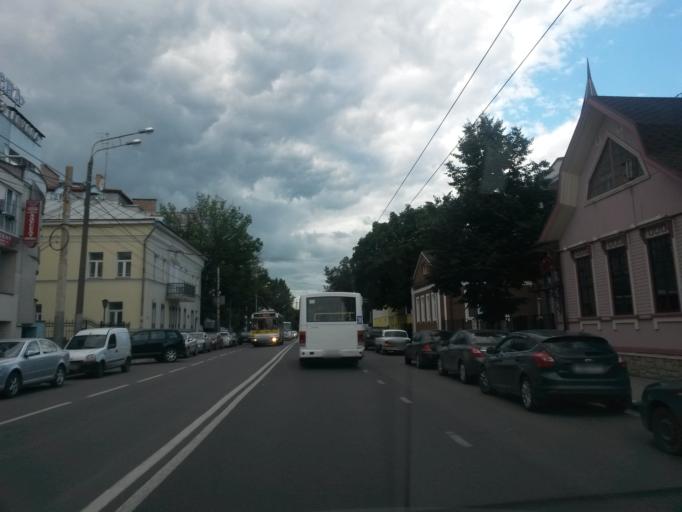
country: RU
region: Jaroslavl
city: Yaroslavl
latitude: 57.6345
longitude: 39.8835
